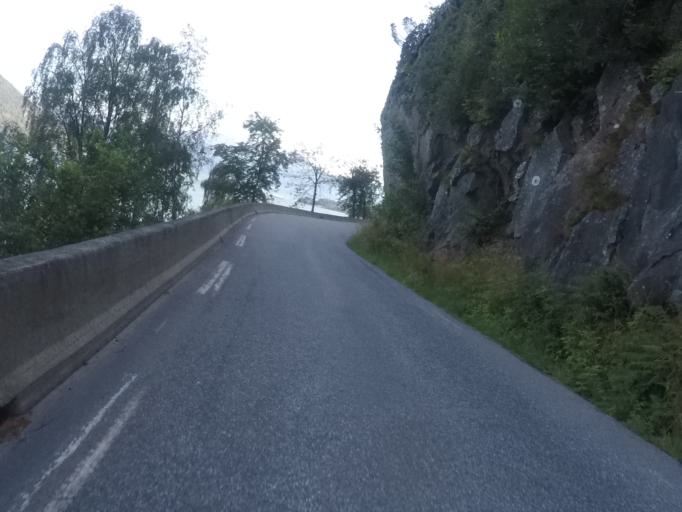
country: NO
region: Sogn og Fjordane
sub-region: Balestrand
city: Balestrand
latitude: 61.2377
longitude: 6.5514
